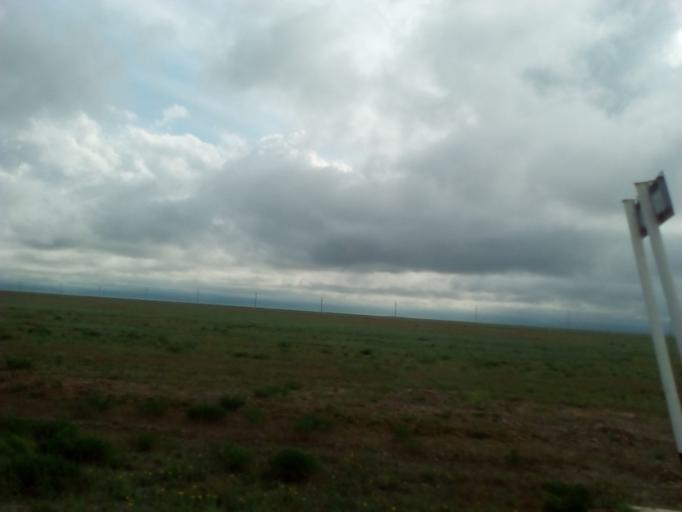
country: KZ
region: Ongtustik Qazaqstan
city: Sholaqqkorghan
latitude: 43.7441
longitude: 69.2013
